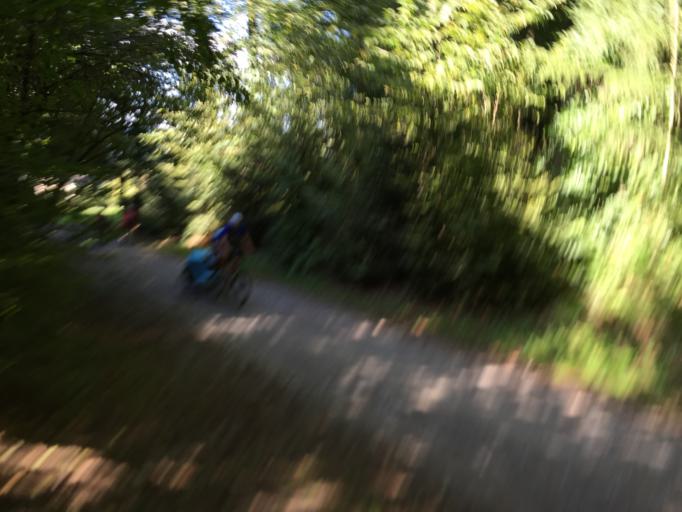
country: CH
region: Bern
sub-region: Bern-Mittelland District
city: Koniz
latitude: 46.9187
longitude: 7.4268
